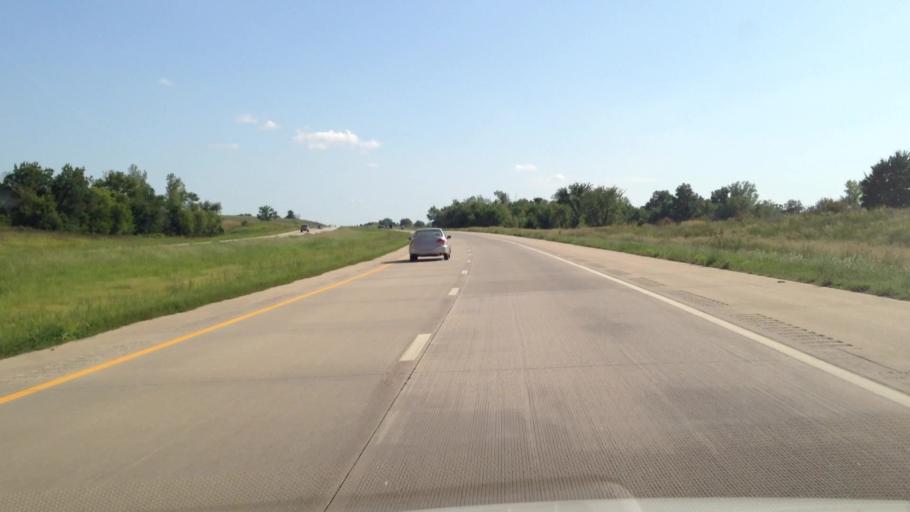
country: US
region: Kansas
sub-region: Bourbon County
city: Fort Scott
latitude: 37.9619
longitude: -94.7090
